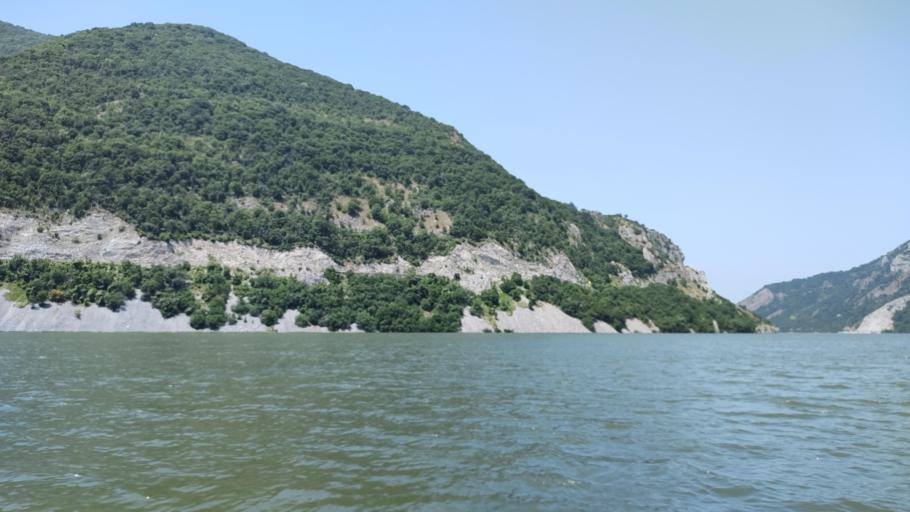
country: RO
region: Caras-Severin
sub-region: Comuna Berzasca
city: Berzasca
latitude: 44.5847
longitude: 22.0270
